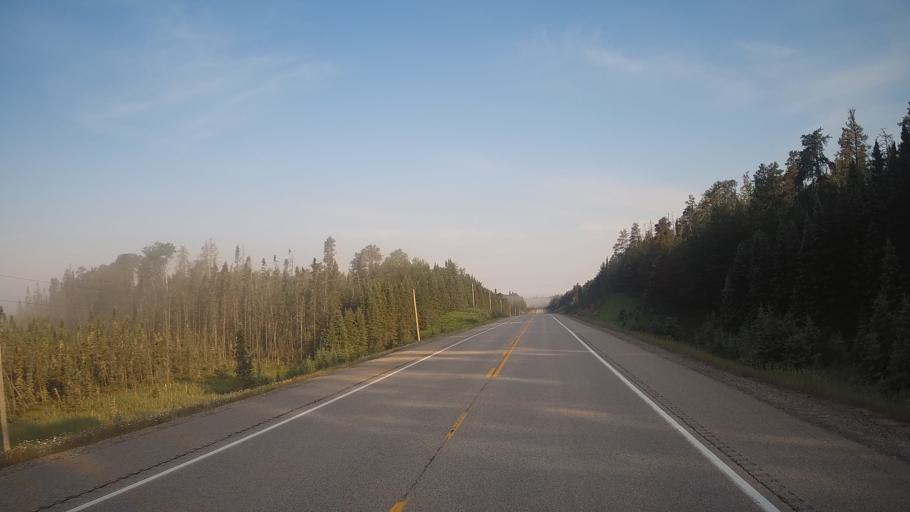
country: CA
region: Ontario
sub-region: Rainy River District
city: Atikokan
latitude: 49.3128
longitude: -91.3759
